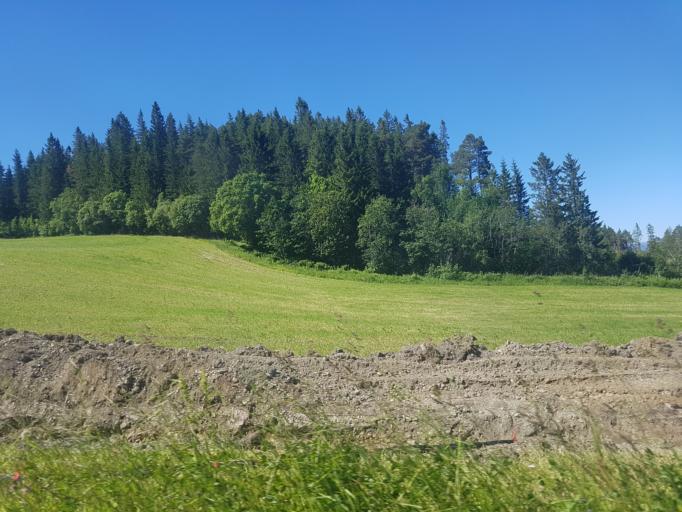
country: NO
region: Sor-Trondelag
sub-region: Skaun
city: Borsa
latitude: 63.4393
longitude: 10.1983
